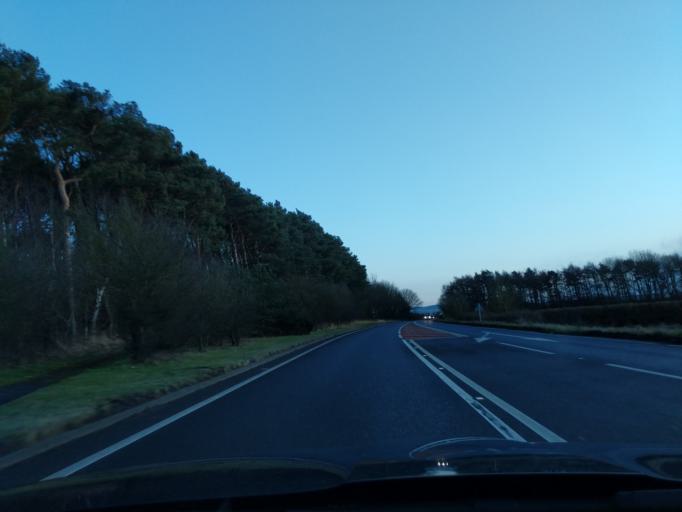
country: GB
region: England
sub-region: Northumberland
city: Ancroft
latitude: 55.7298
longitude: -1.9873
